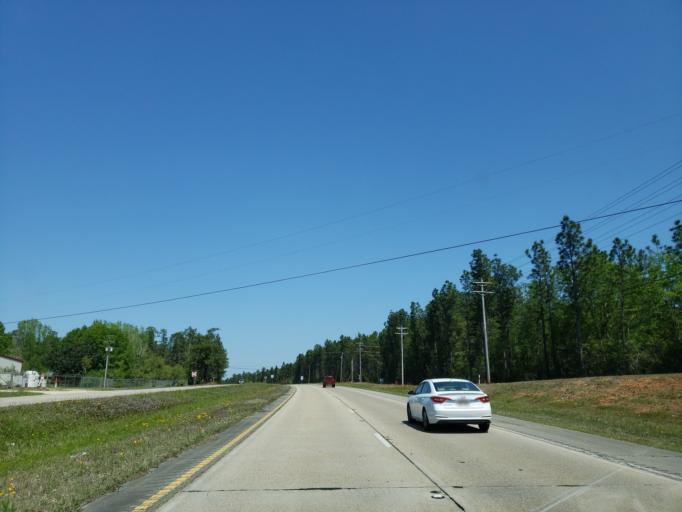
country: US
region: Mississippi
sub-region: Harrison County
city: Saucier
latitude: 30.6014
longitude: -89.1273
